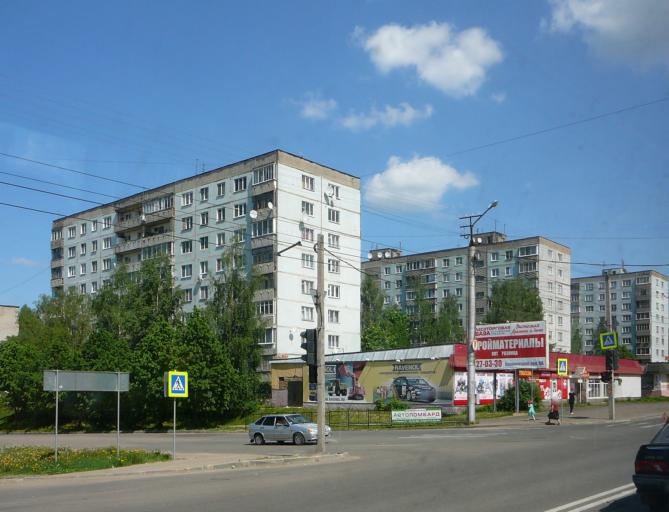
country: RU
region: Smolensk
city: Smolensk
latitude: 54.7681
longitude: 32.0122
